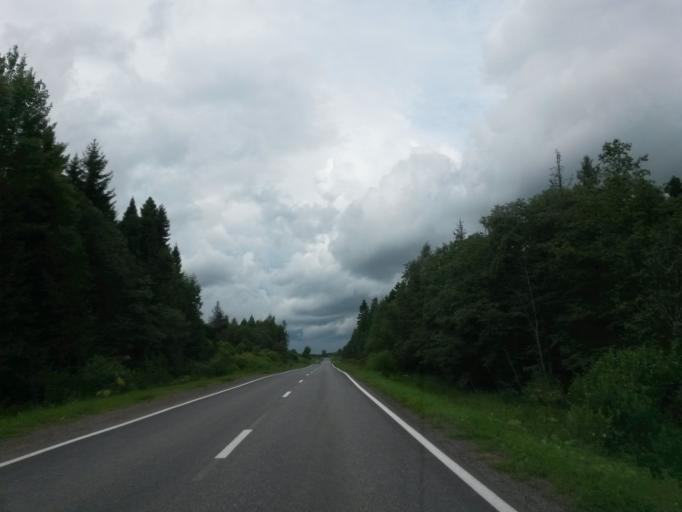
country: RU
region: Jaroslavl
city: Konstantinovskiy
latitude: 57.8260
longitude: 39.6772
